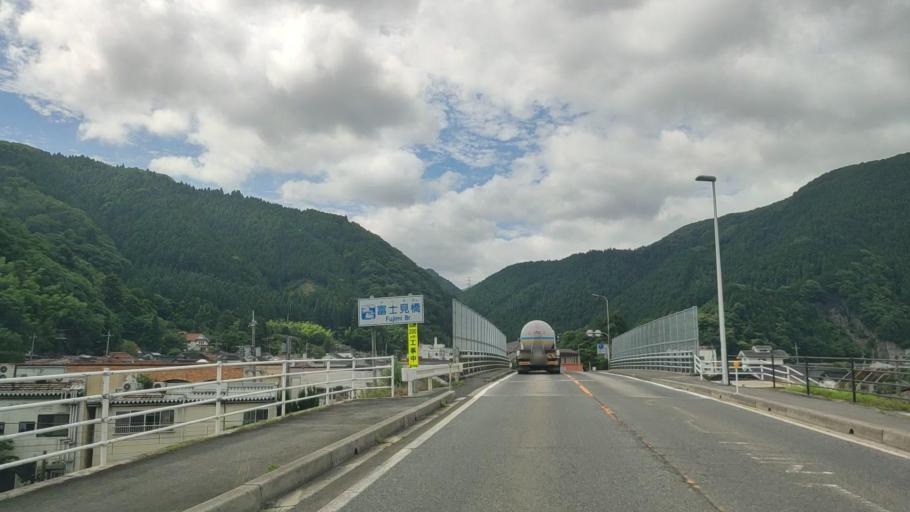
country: JP
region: Tottori
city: Yonago
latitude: 35.2408
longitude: 133.4403
